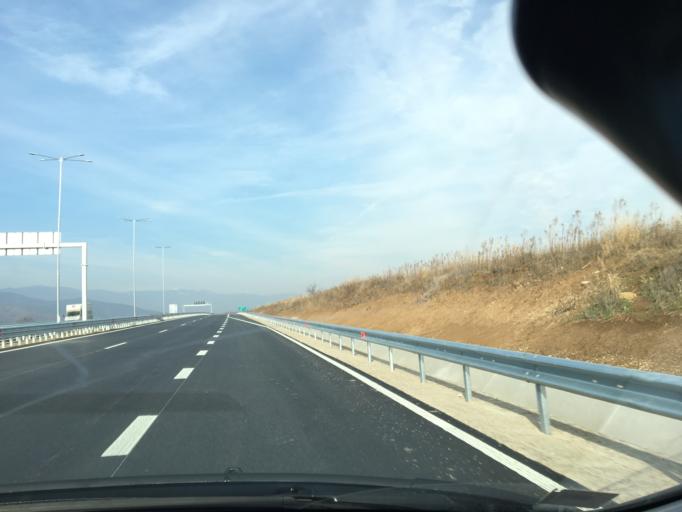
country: BG
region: Blagoevgrad
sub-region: Obshtina Sandanski
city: Sandanski
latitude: 41.5446
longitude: 23.2555
